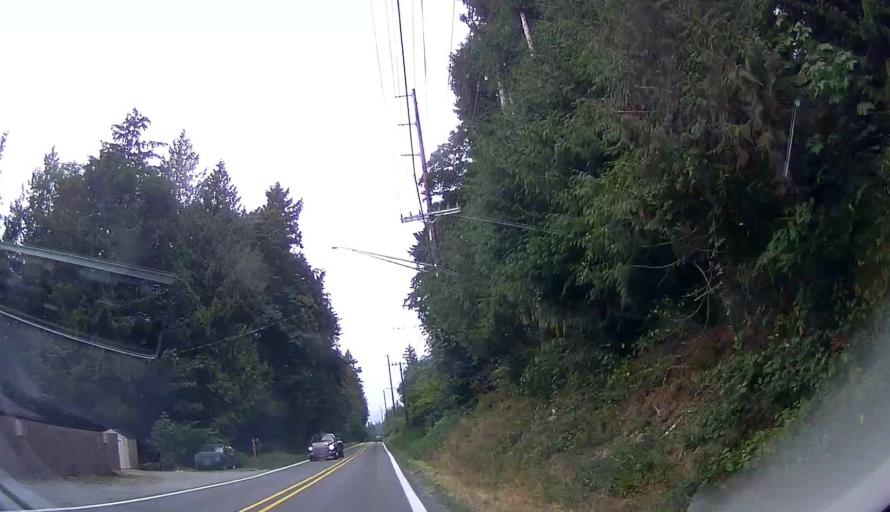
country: US
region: Washington
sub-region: Snohomish County
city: Warm Beach
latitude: 48.1923
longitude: -122.3409
